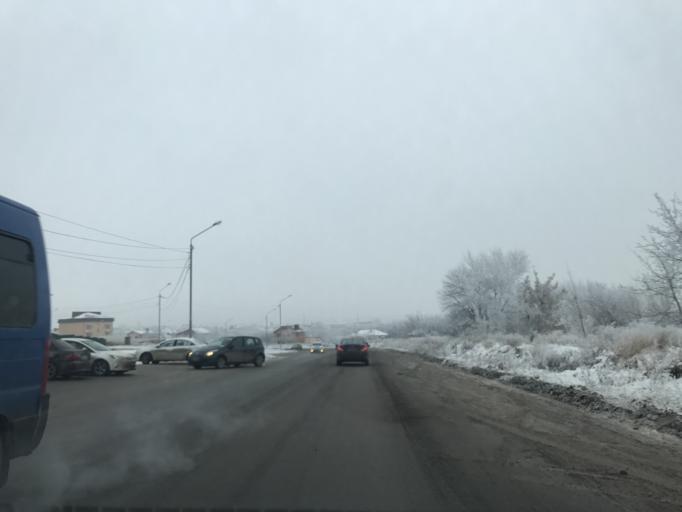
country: RU
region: Rostov
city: Aksay
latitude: 47.2439
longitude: 39.8334
